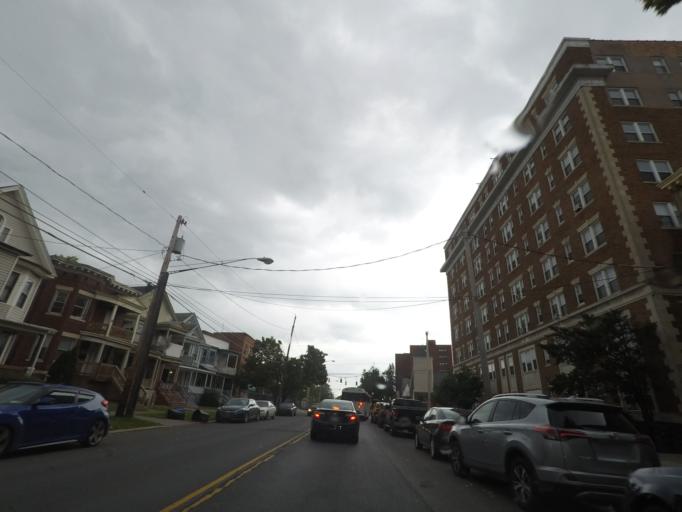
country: US
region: New York
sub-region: Albany County
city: Albany
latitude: 42.6612
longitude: -73.7751
